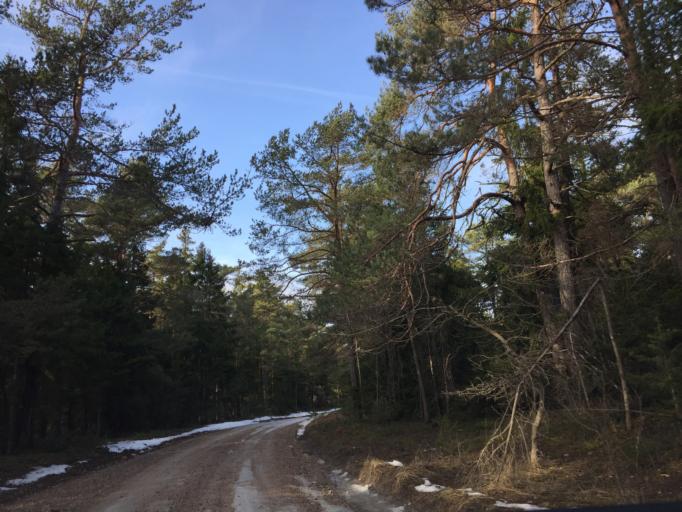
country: EE
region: Saare
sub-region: Kuressaare linn
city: Kuressaare
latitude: 58.4745
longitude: 21.9563
